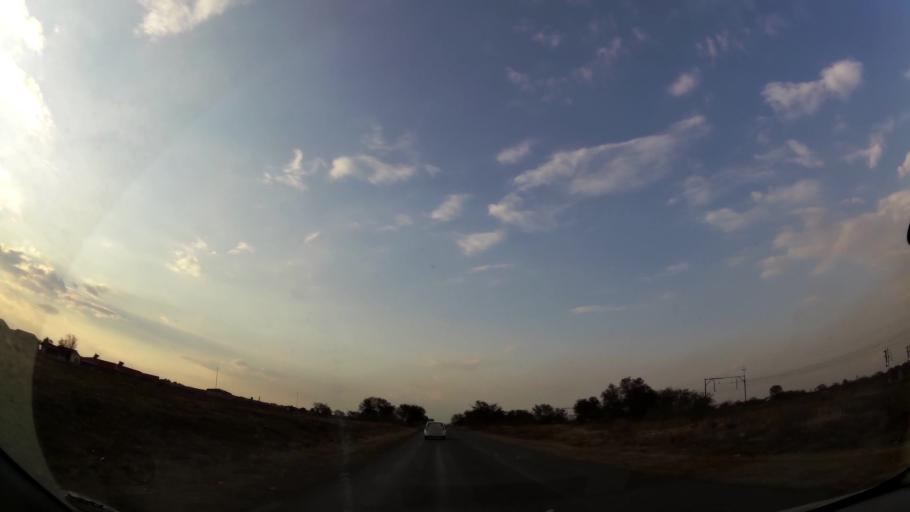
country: ZA
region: Gauteng
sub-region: City of Johannesburg Metropolitan Municipality
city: Orange Farm
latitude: -26.5799
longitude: 27.8564
